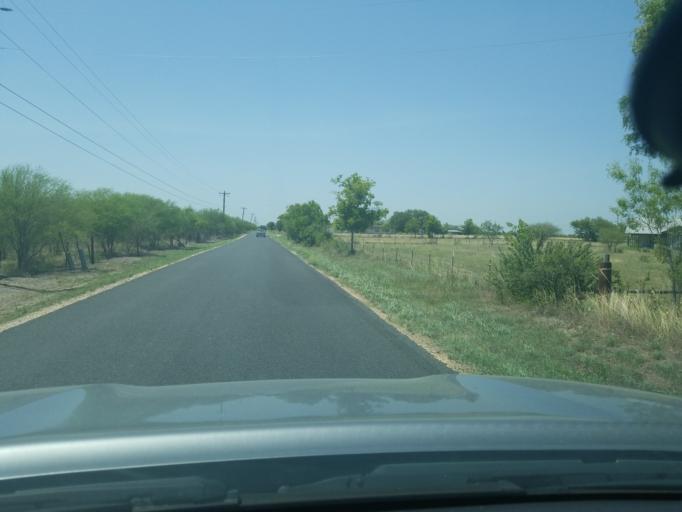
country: US
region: Texas
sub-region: Guadalupe County
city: Marion
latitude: 29.5817
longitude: -98.1700
